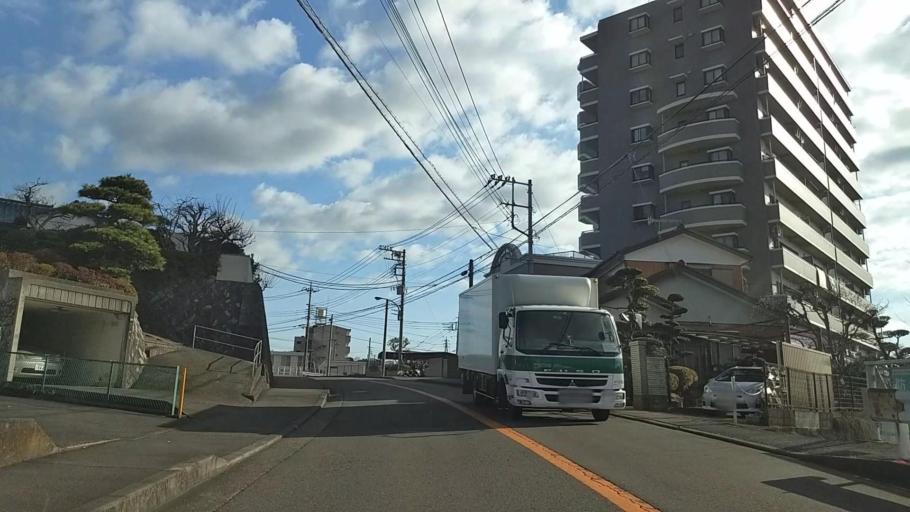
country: JP
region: Kanagawa
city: Atsugi
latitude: 35.4329
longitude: 139.3350
